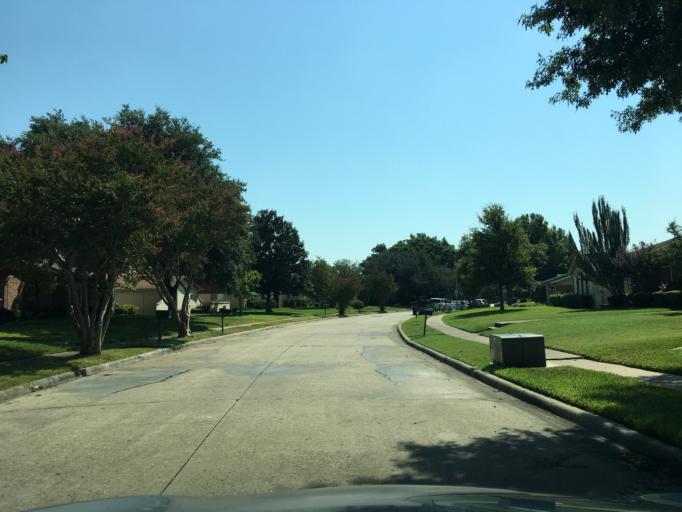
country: US
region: Texas
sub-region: Dallas County
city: Garland
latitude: 32.9339
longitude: -96.6516
